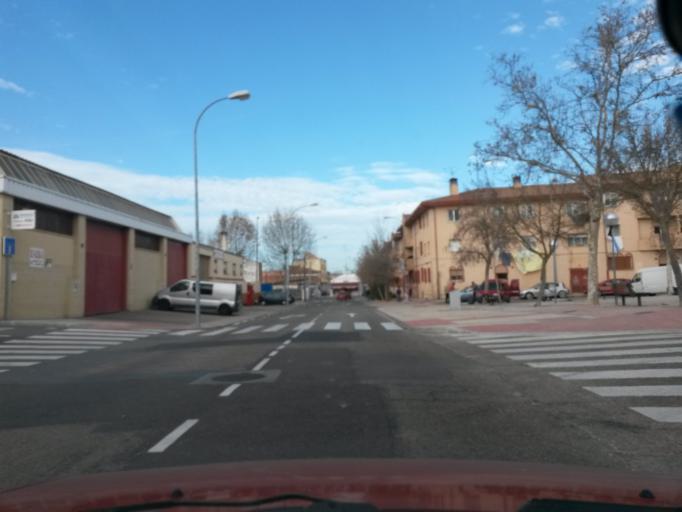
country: ES
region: Castille and Leon
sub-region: Provincia de Salamanca
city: Salamanca
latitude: 40.9728
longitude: -5.6395
